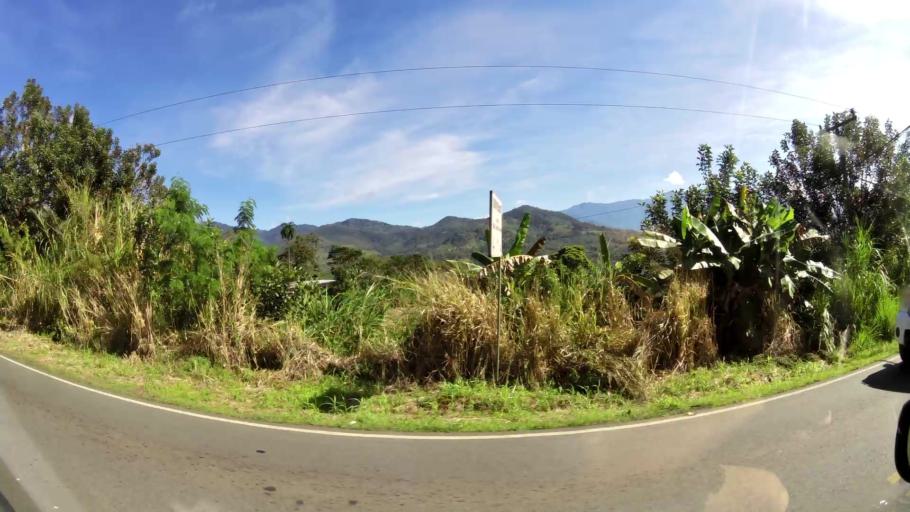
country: CR
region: San Jose
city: San Isidro
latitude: 9.4089
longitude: -83.7113
